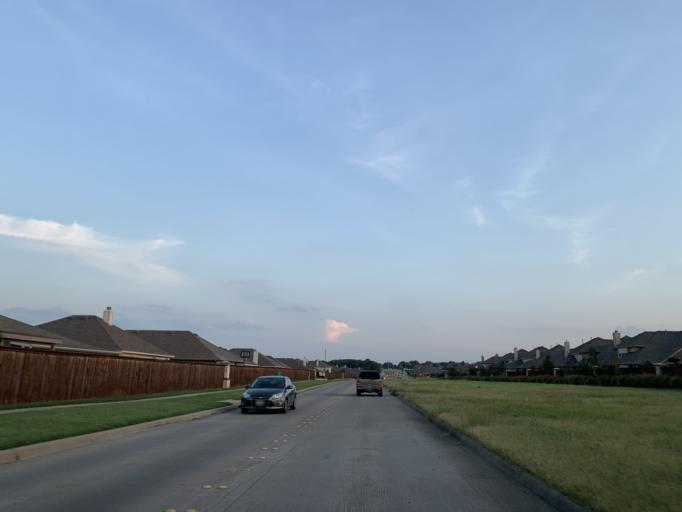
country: US
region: Texas
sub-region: Tarrant County
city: Keller
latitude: 32.9598
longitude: -97.2645
